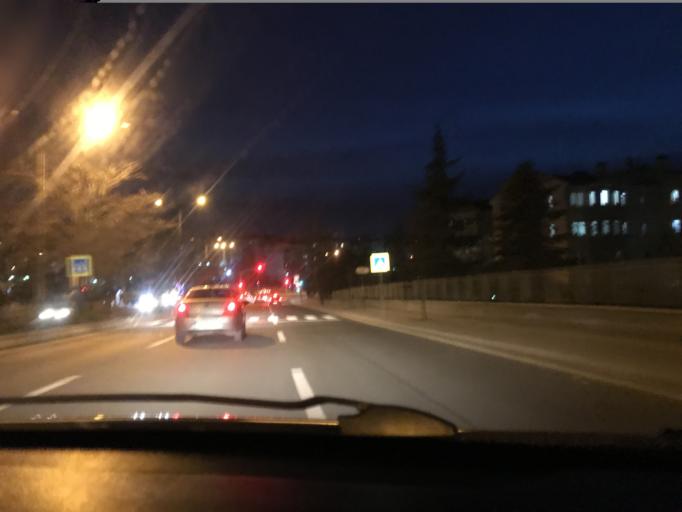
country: TR
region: Ankara
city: Batikent
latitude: 39.9594
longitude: 32.7300
